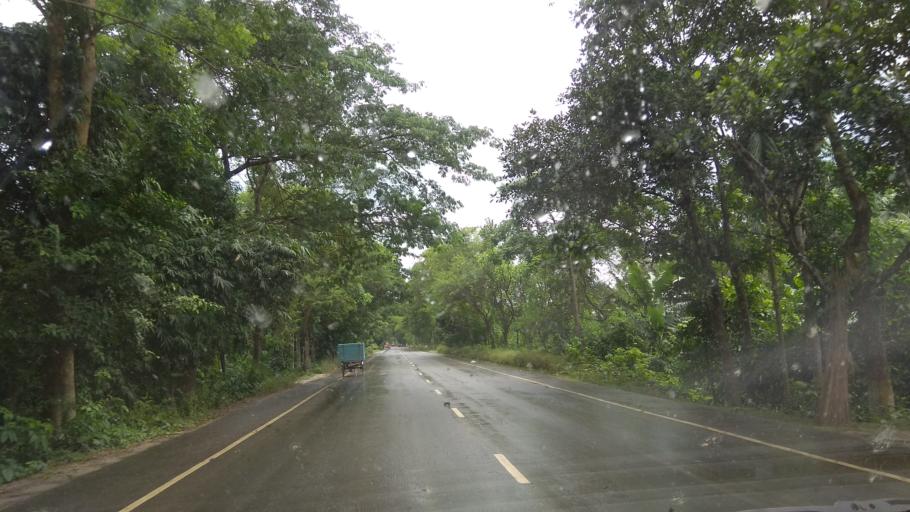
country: BD
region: Khulna
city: Kalia
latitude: 23.2471
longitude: 89.7562
